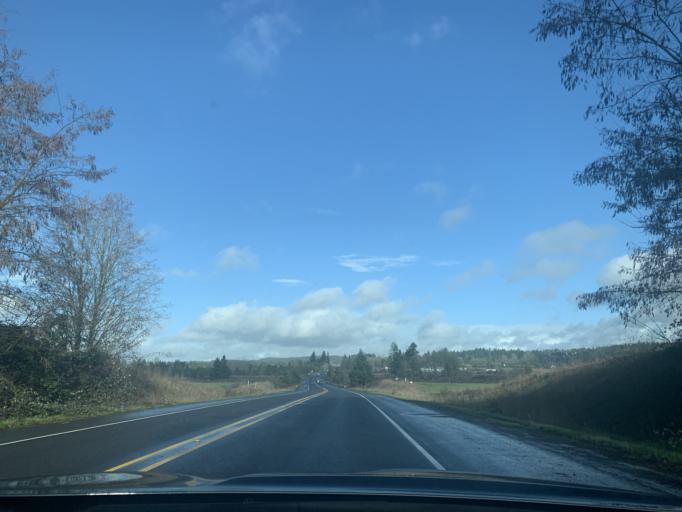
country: US
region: Oregon
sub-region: Washington County
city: Sherwood
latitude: 45.3904
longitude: -122.8518
